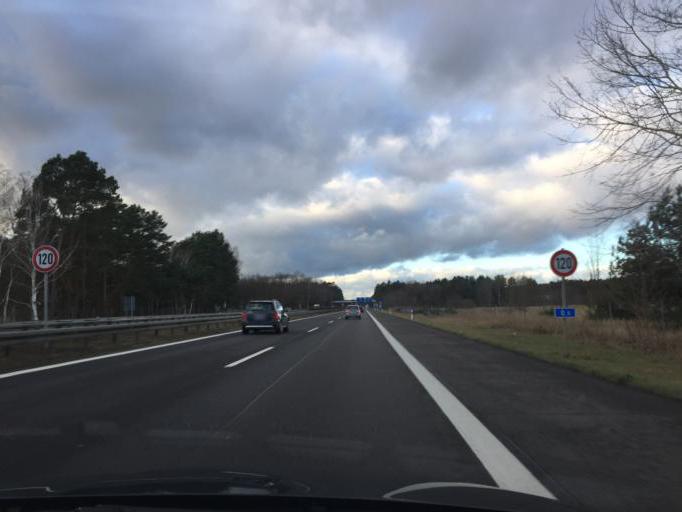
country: DE
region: Brandenburg
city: Lubbenau
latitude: 51.8418
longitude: 13.9314
